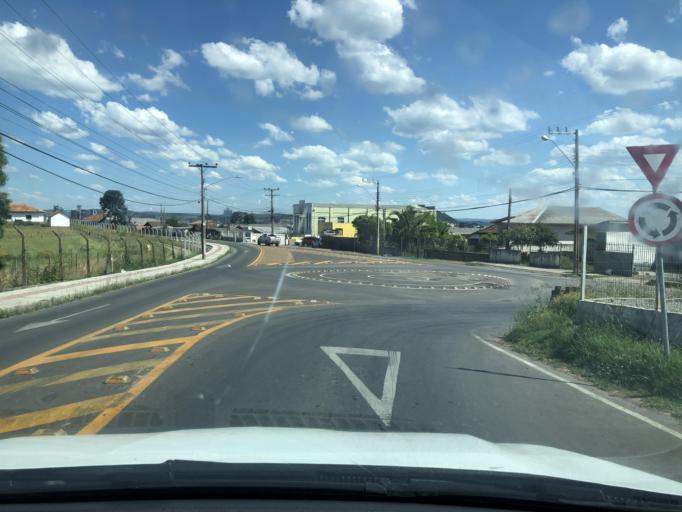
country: BR
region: Santa Catarina
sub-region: Lages
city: Lages
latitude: -27.8078
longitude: -50.3362
